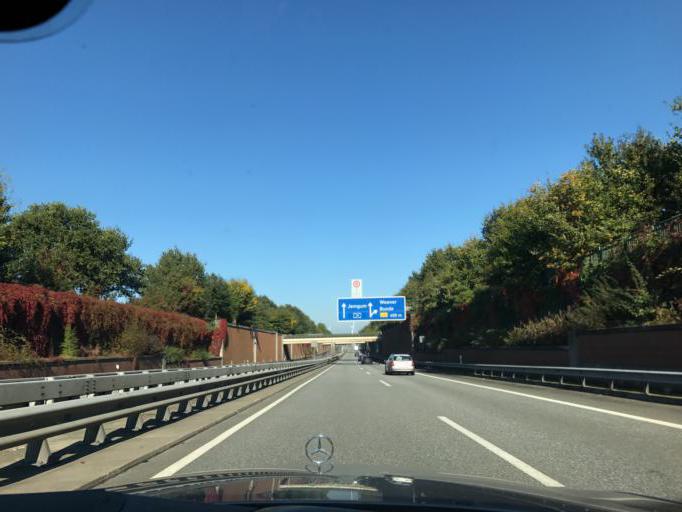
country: DE
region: Lower Saxony
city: Bunde
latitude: 53.1741
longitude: 7.2899
